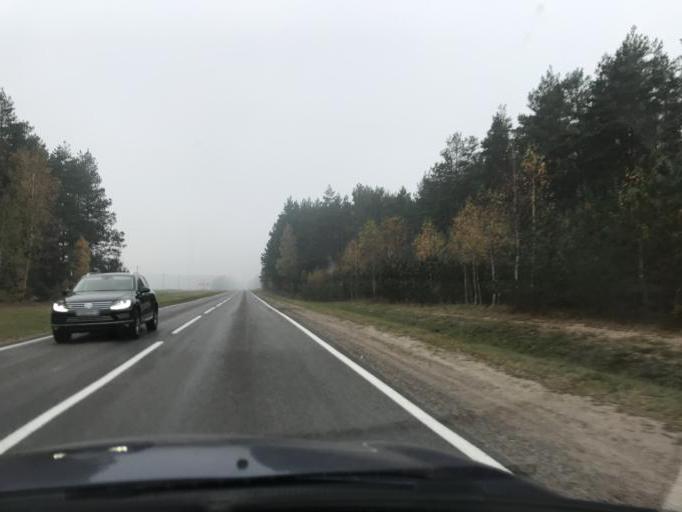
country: BY
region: Grodnenskaya
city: Hrodna
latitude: 53.7812
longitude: 23.8489
